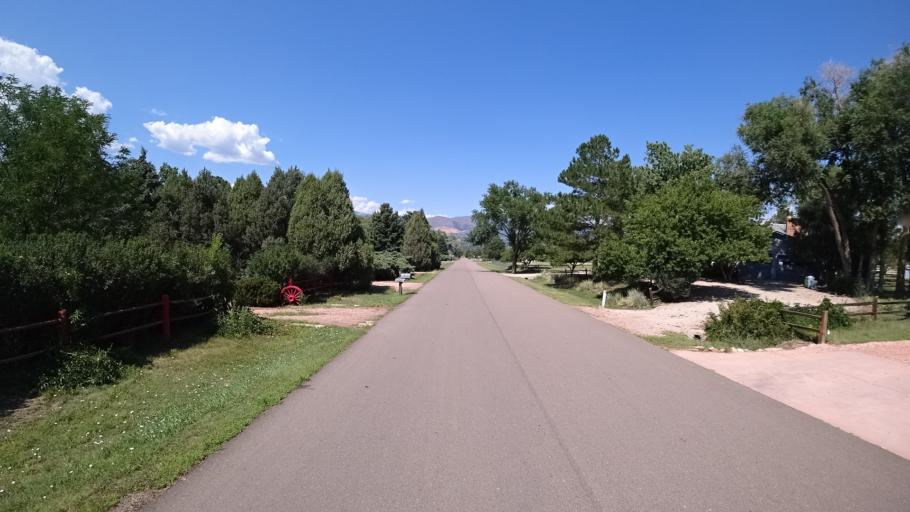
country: US
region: Colorado
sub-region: El Paso County
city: Air Force Academy
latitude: 38.9396
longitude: -104.7861
